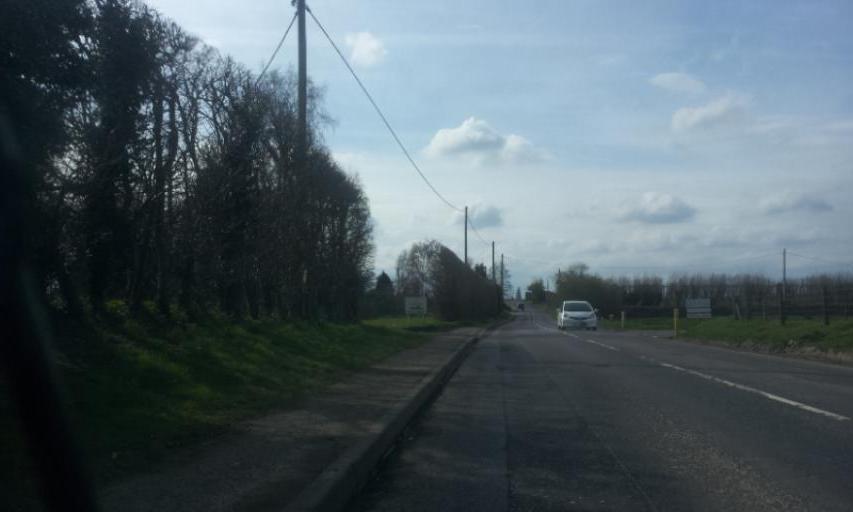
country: GB
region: England
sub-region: Kent
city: Faversham
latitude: 51.3116
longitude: 0.9212
